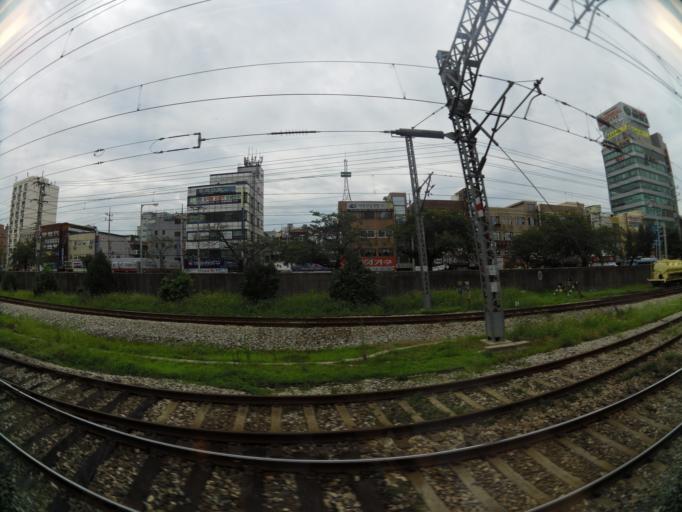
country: KR
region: Gyeonggi-do
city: Anyang-si
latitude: 37.3700
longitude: 126.9444
